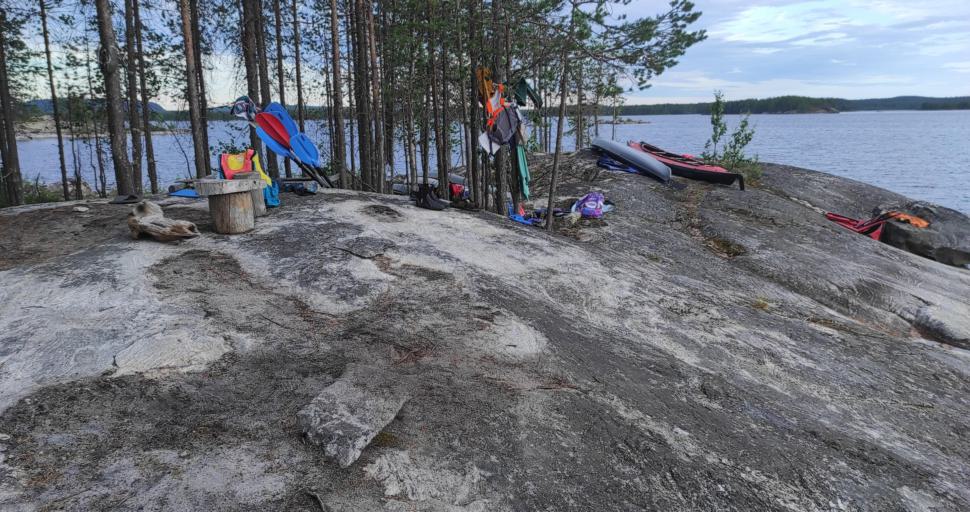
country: RU
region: Murmansk
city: Zelenoborskiy
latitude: 66.6816
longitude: 32.4269
